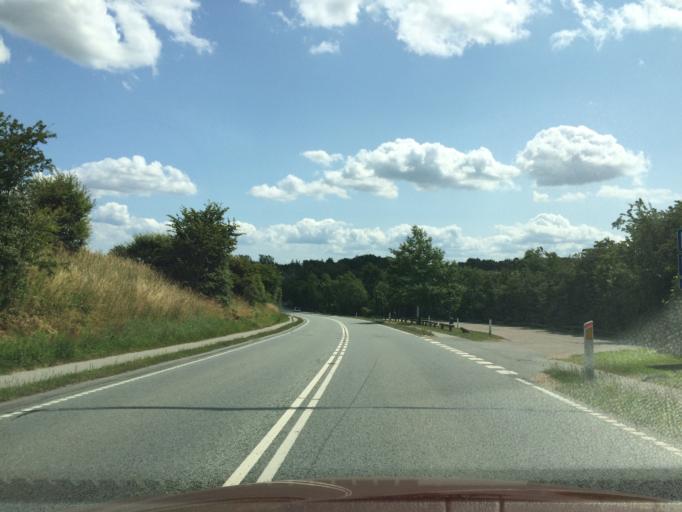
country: DK
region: Central Jutland
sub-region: Arhus Kommune
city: Sabro
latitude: 56.2158
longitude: 9.9926
